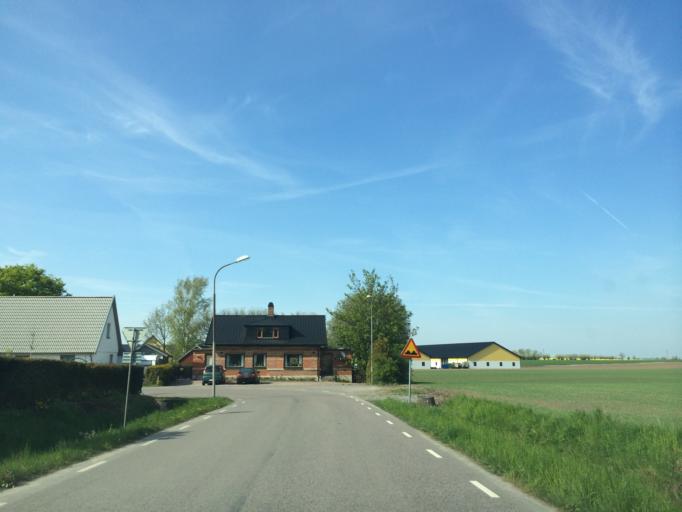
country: SE
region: Skane
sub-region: Kavlinge Kommun
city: Kaevlinge
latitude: 55.7266
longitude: 13.1085
